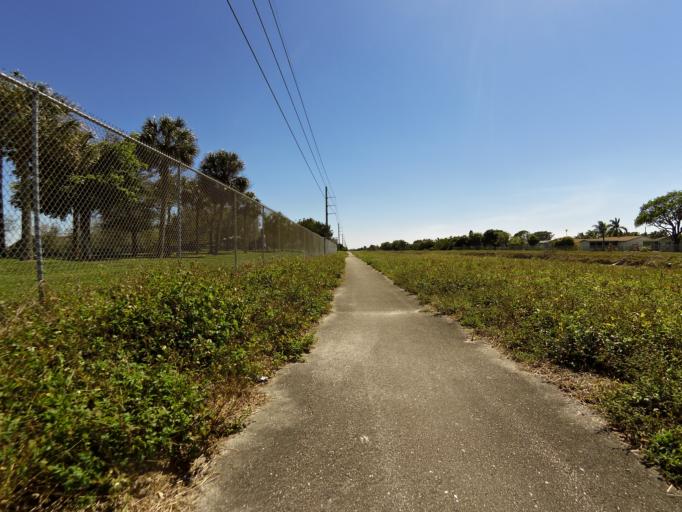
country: US
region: Florida
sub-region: Broward County
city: Tamarac
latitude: 26.1775
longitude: -80.2977
